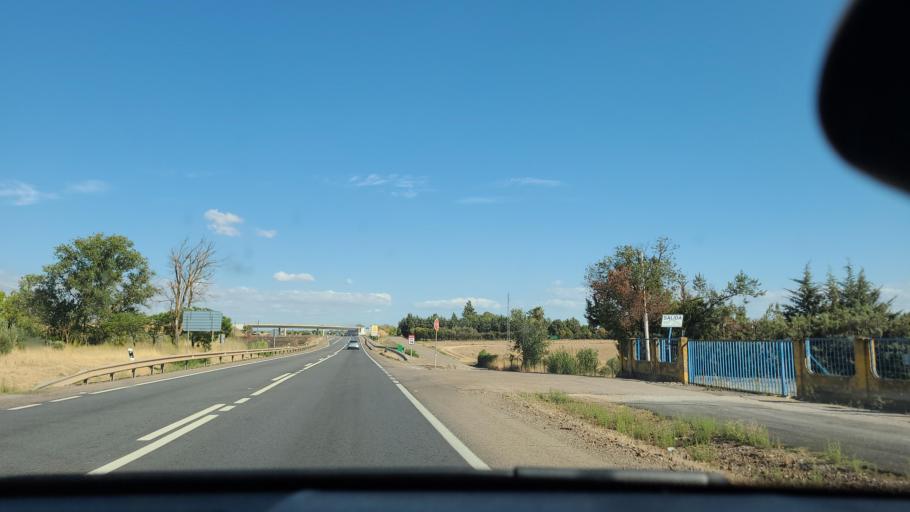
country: ES
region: Extremadura
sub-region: Provincia de Badajoz
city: Puebla de Sancho Perez
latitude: 38.4002
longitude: -6.3526
